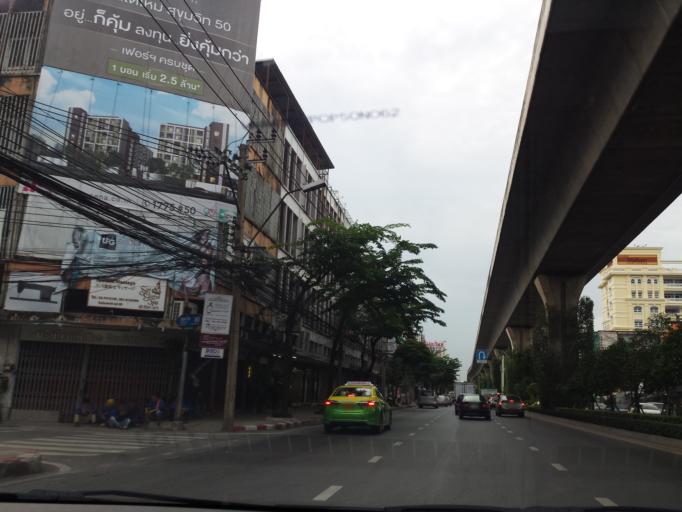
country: TH
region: Bangkok
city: Phra Khanong
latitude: 13.6989
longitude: 100.6042
